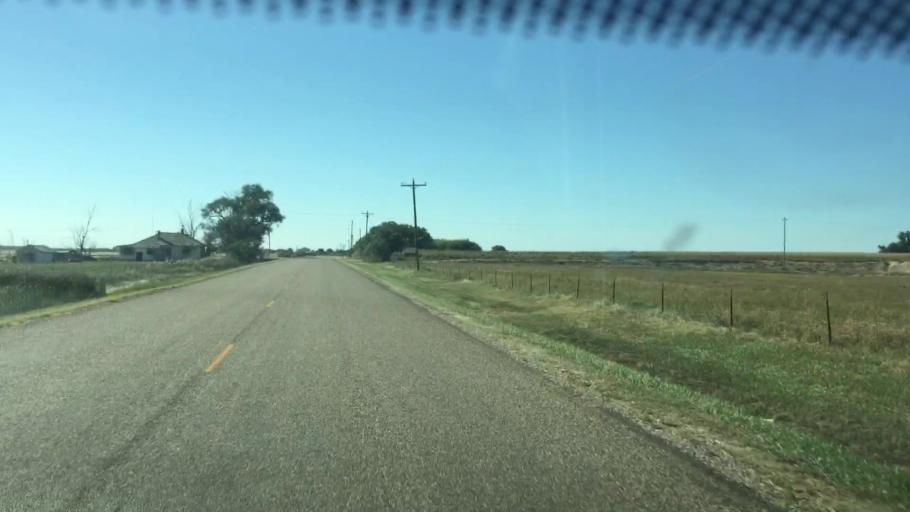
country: US
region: Colorado
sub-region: Prowers County
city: Lamar
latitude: 38.1158
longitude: -102.5920
